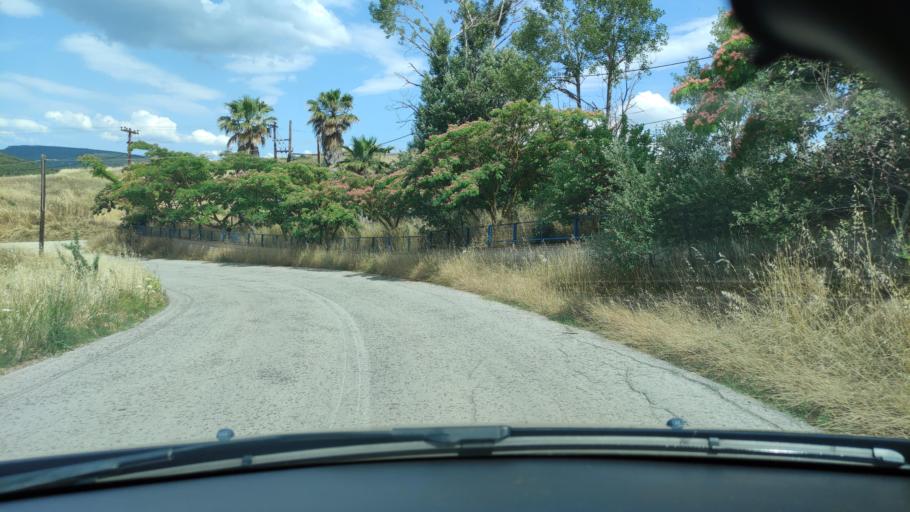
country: GR
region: Central Greece
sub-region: Nomos Evvoias
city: Afration
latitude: 38.5202
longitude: 23.7338
